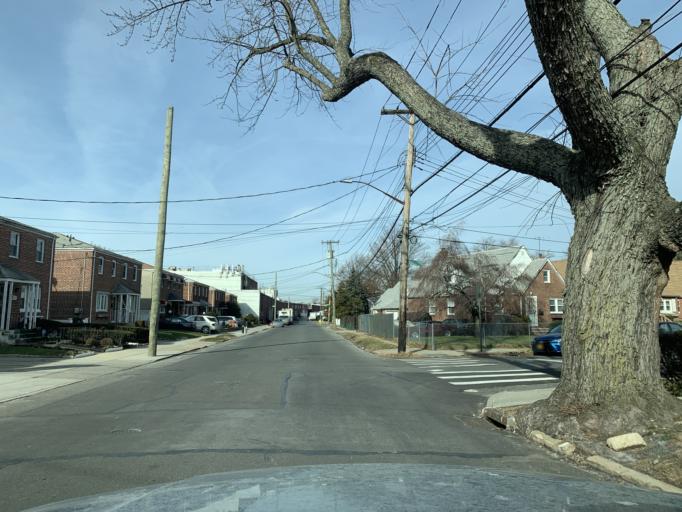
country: US
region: New York
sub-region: Queens County
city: Jamaica
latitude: 40.6970
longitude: -73.7695
